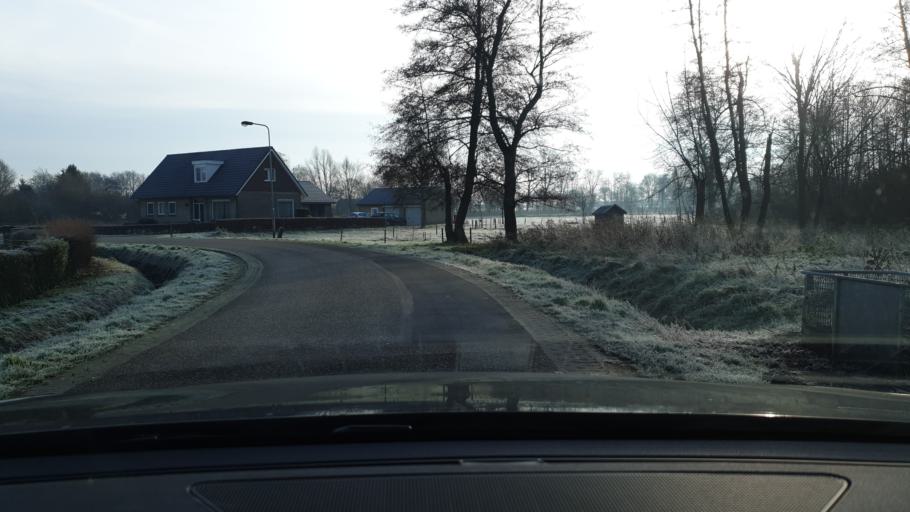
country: NL
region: Limburg
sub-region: Gemeente Peel en Maas
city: Maasbree
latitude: 51.4315
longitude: 6.0450
